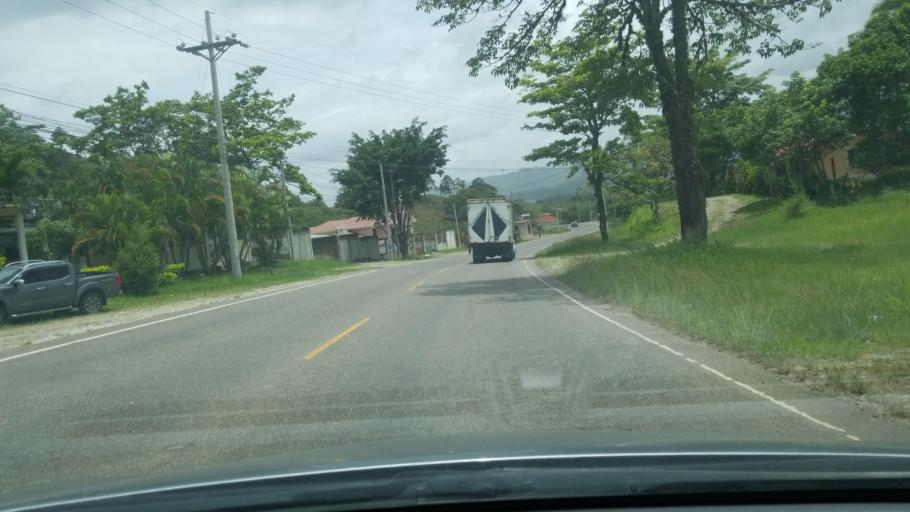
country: HN
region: Copan
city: Cucuyagua
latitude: 14.6663
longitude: -88.8672
